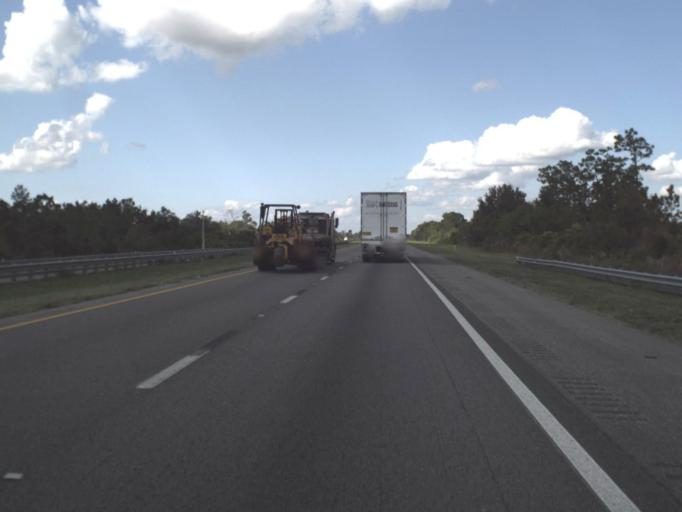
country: US
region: Florida
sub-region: Indian River County
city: Fellsmere
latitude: 27.7639
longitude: -80.9527
